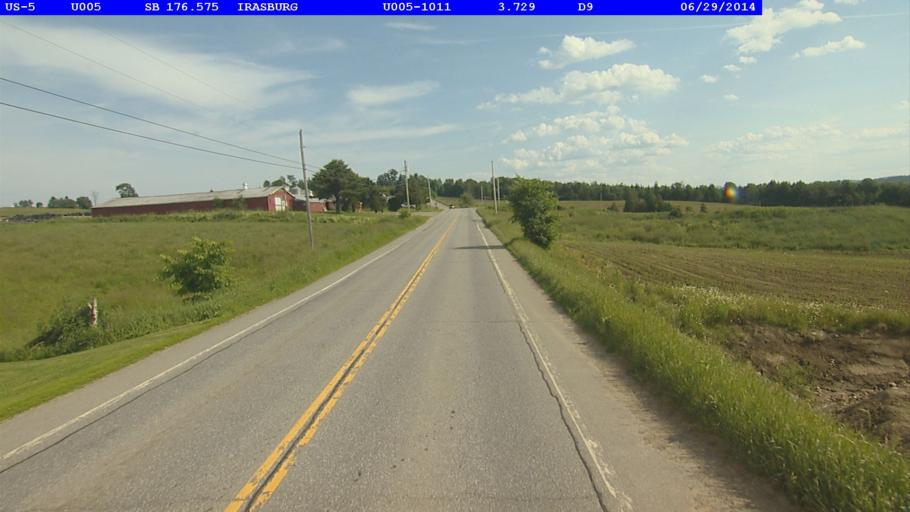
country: US
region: Vermont
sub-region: Orleans County
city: Newport
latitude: 44.8456
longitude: -72.2620
